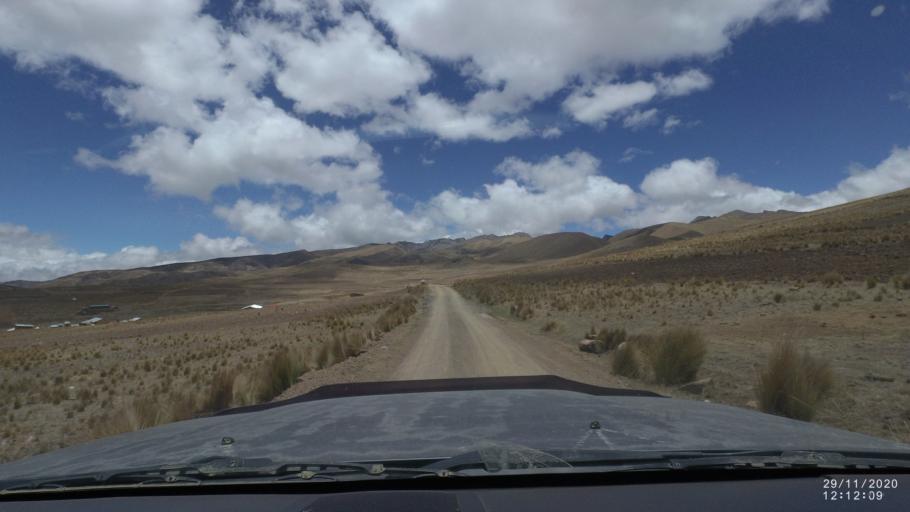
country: BO
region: Cochabamba
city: Cochabamba
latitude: -17.1145
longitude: -66.3034
